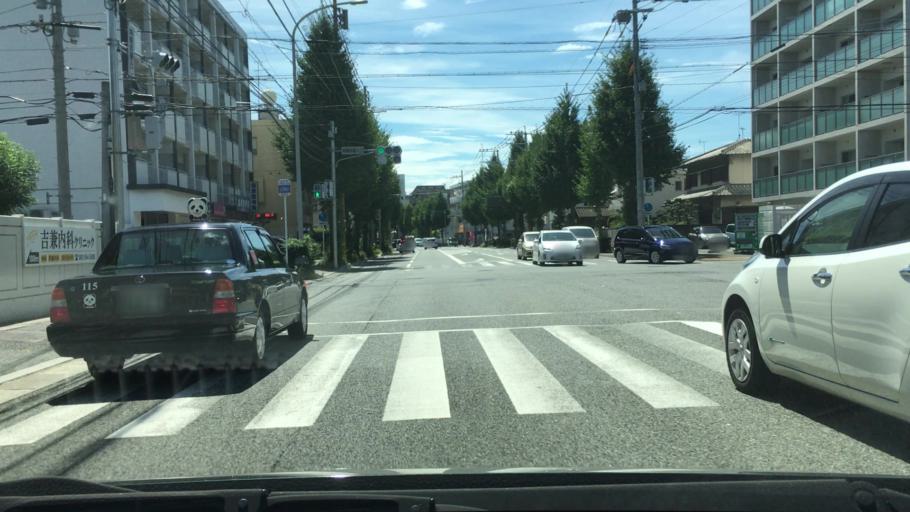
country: JP
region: Fukuoka
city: Fukuoka-shi
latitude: 33.5664
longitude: 130.4278
